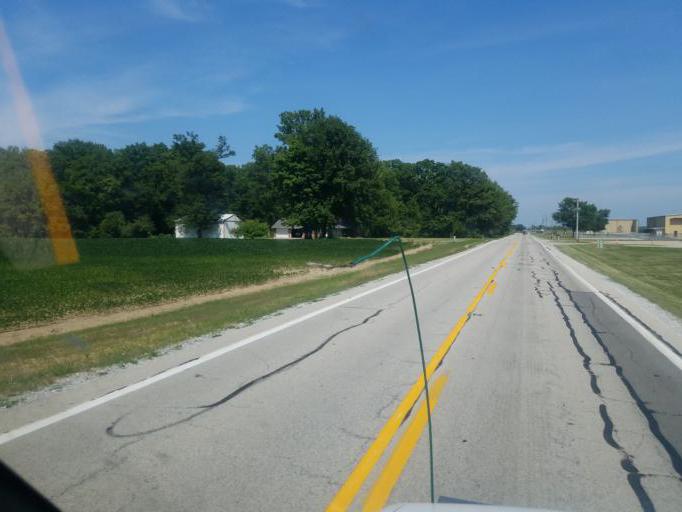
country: US
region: Ohio
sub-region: Auglaize County
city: New Bremen
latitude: 40.4960
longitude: -84.3032
